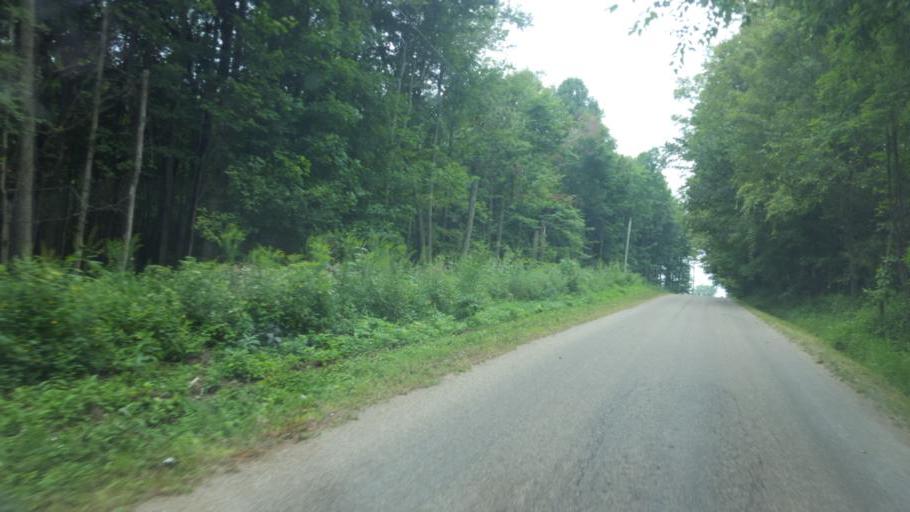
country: US
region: Ohio
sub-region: Richland County
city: Lexington
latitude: 40.6611
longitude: -82.6517
